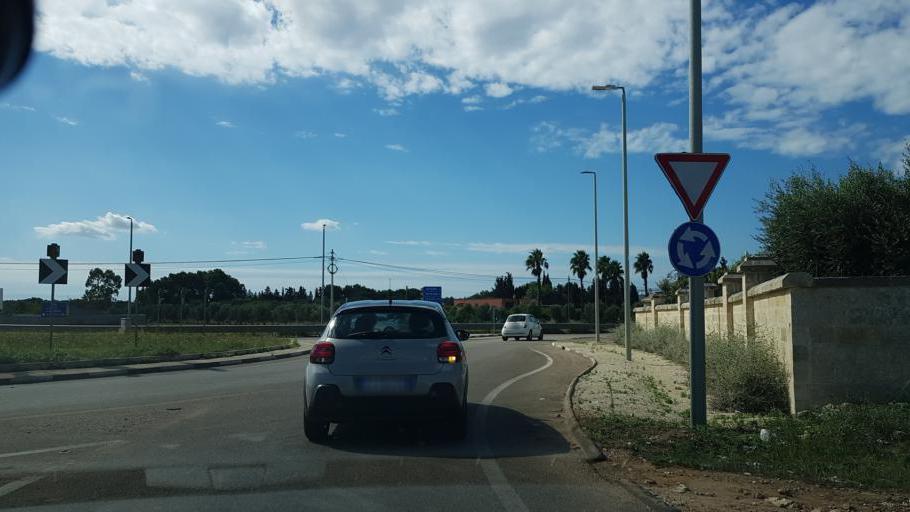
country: IT
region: Apulia
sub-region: Provincia di Lecce
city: Leverano
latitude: 40.2869
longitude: 17.9690
